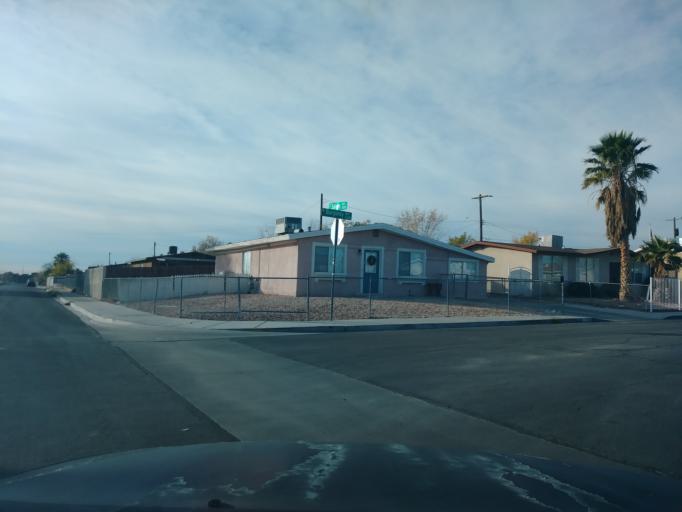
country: US
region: Nevada
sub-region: Clark County
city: Spring Valley
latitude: 36.1657
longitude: -115.2281
